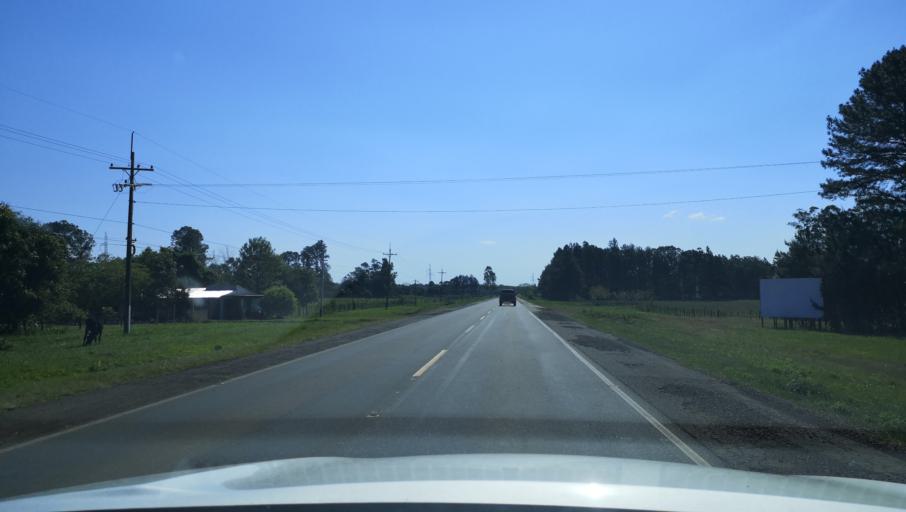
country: PY
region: Itapua
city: General Delgado
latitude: -27.0738
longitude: -56.5947
